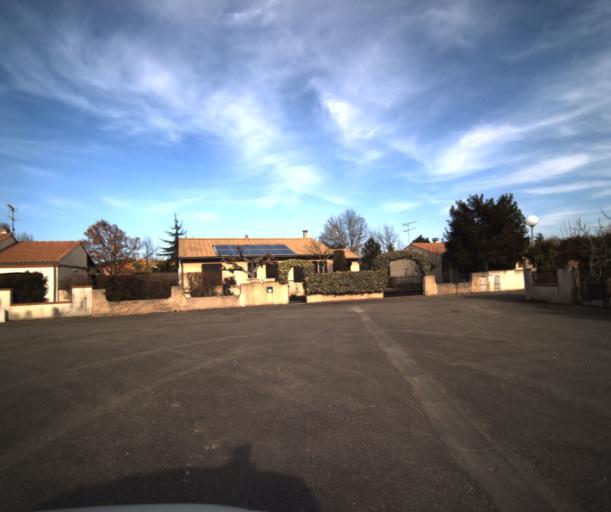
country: FR
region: Midi-Pyrenees
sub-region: Departement du Tarn-et-Garonne
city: Labastide-Saint-Pierre
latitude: 43.9193
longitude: 1.3599
